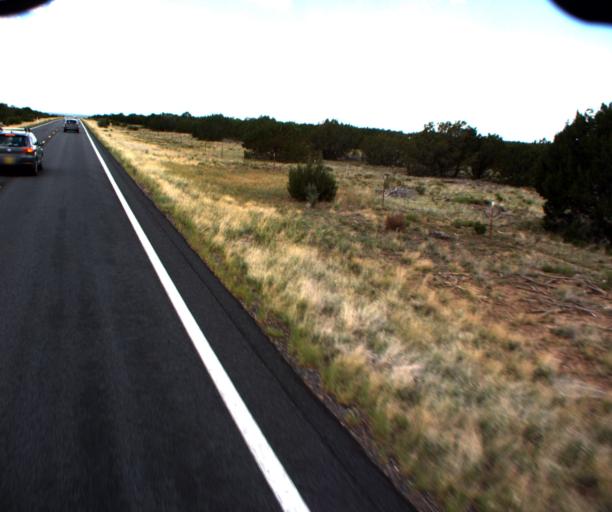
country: US
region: Arizona
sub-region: Coconino County
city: Parks
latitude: 35.5788
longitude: -111.9433
